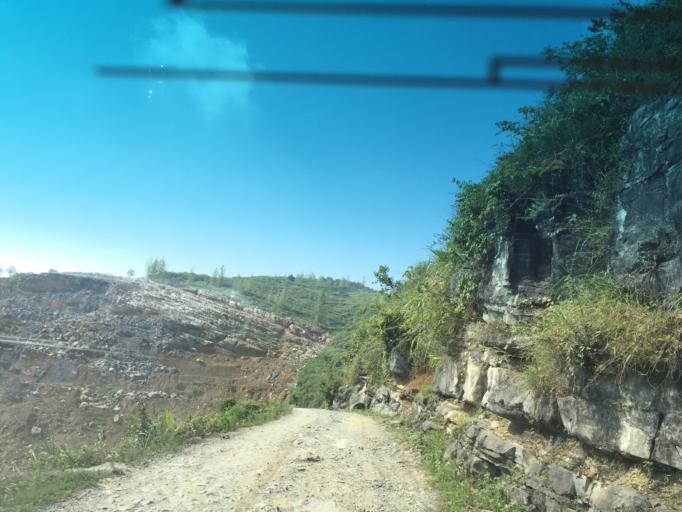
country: CN
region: Guizhou Sheng
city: Longquan
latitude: 28.2765
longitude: 108.0325
